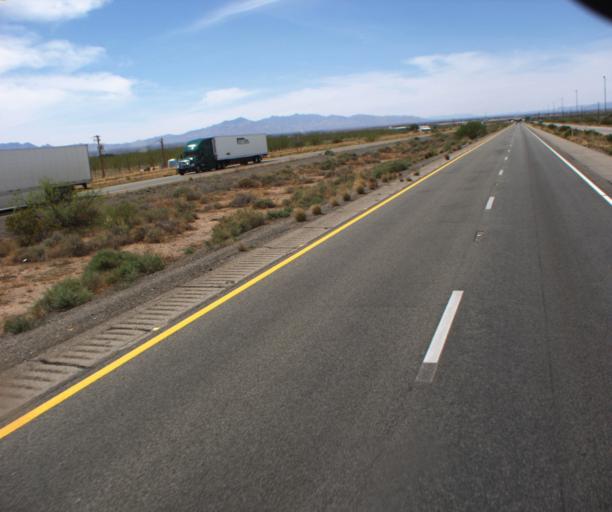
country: US
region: New Mexico
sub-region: Hidalgo County
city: Lordsburg
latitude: 32.2548
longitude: -109.1666
